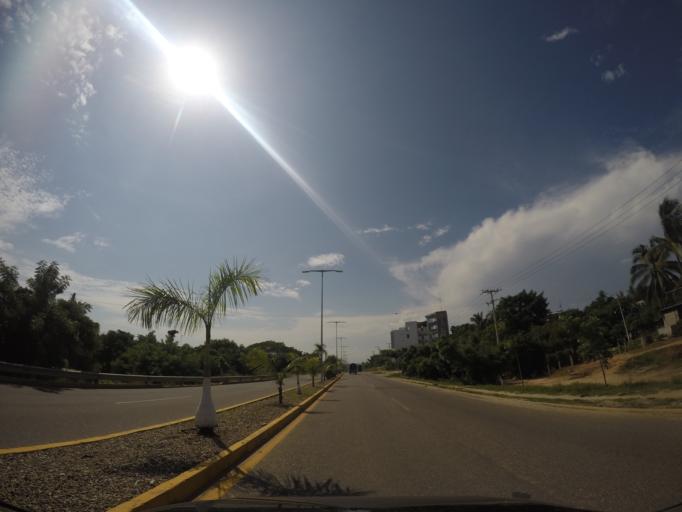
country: MX
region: Oaxaca
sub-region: Santa Maria Colotepec
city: Brisas de Zicatela
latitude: 15.8491
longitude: -97.0494
